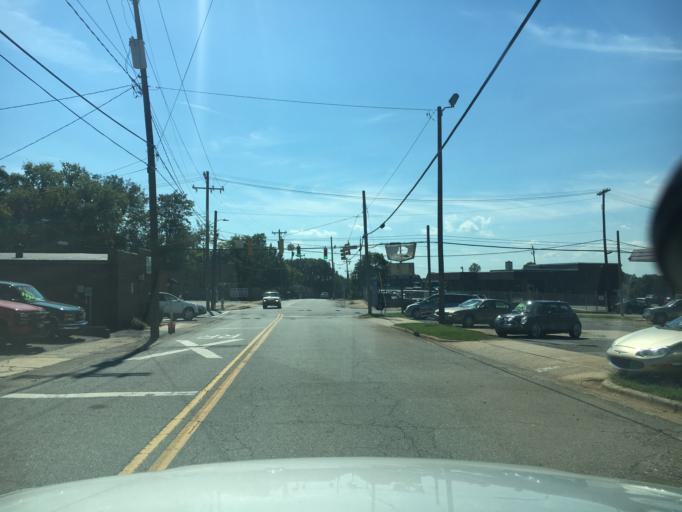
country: US
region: North Carolina
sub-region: Catawba County
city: Hickory
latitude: 35.7315
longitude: -81.3525
